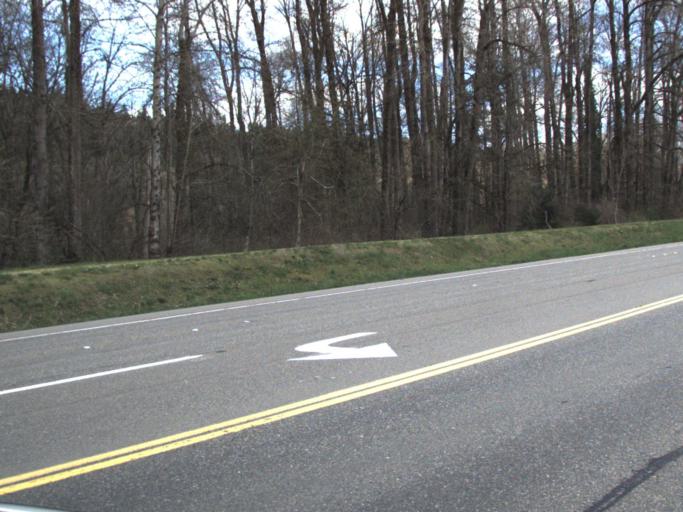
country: US
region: Washington
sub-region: King County
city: Fairwood
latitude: 47.4648
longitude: -122.1349
